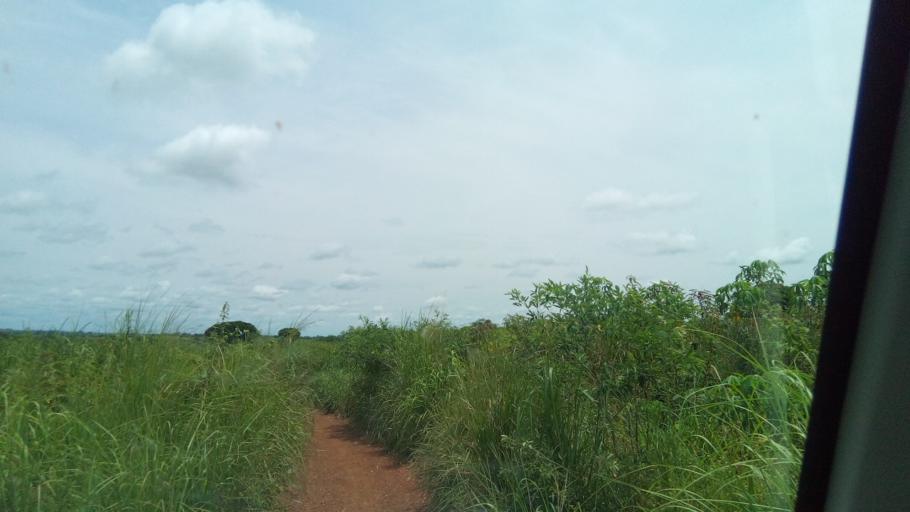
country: AO
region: Zaire
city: Mbanza Congo
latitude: -5.7911
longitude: 13.9922
